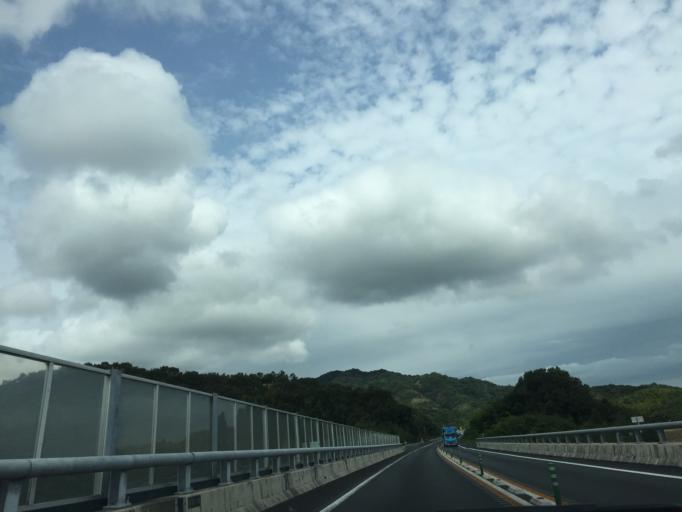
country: JP
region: Kagawa
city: Shido
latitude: 34.2490
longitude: 134.2957
